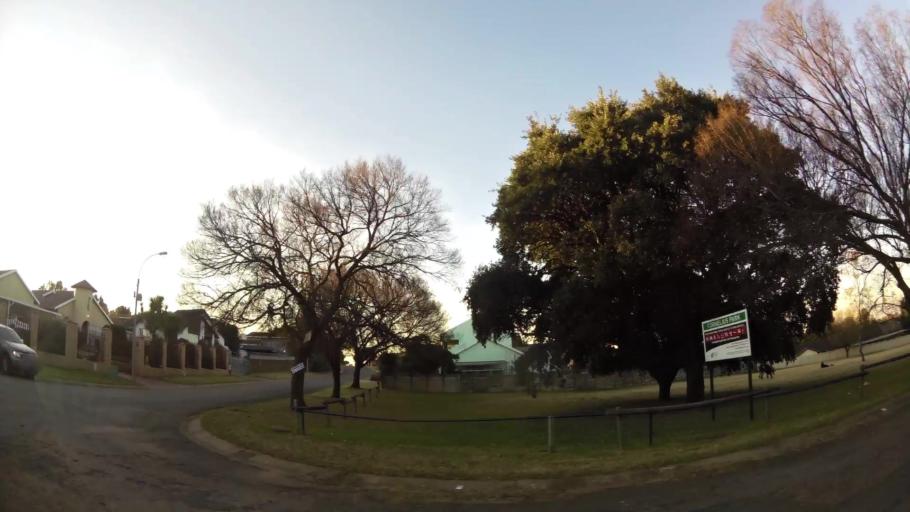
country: ZA
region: Gauteng
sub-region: City of Johannesburg Metropolitan Municipality
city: Roodepoort
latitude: -26.1520
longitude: 27.8954
